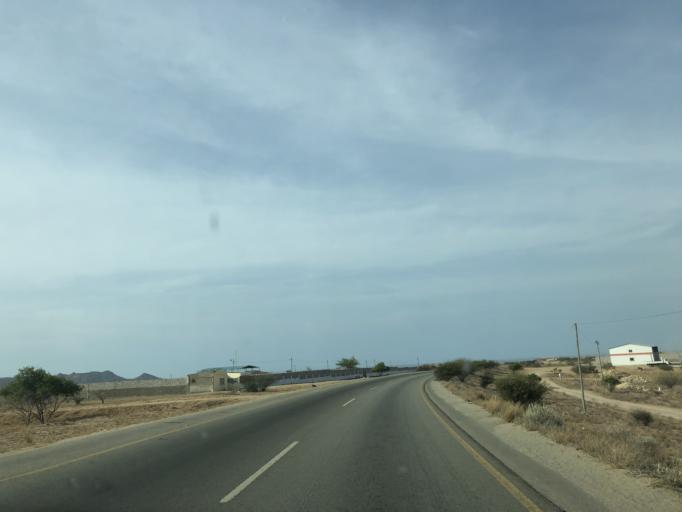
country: AO
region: Benguela
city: Benguela
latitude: -12.6862
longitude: 13.3410
